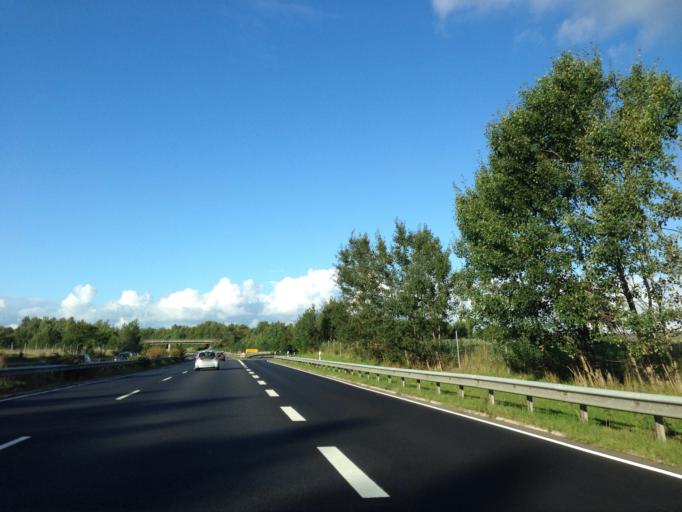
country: DE
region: Lower Saxony
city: Wendisch Evern
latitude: 53.2255
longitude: 10.4492
